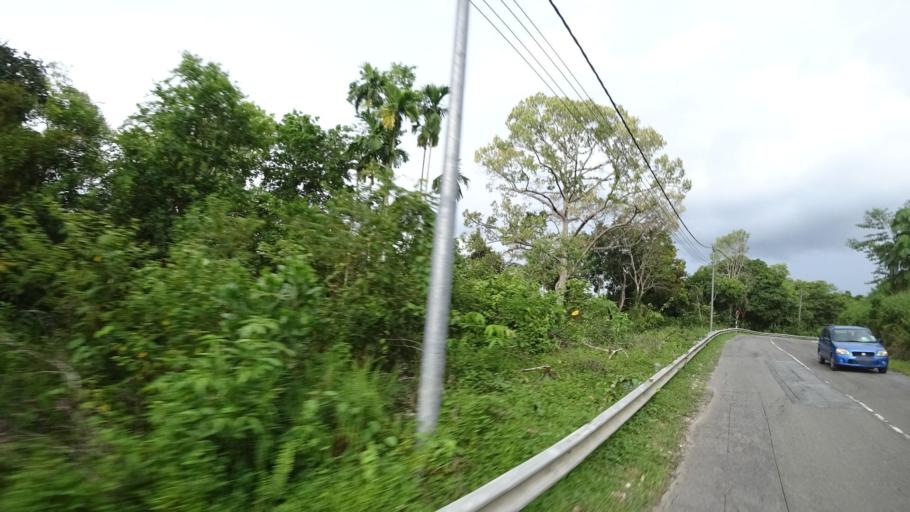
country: BN
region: Brunei and Muara
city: Bandar Seri Begawan
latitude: 4.8578
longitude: 114.9532
